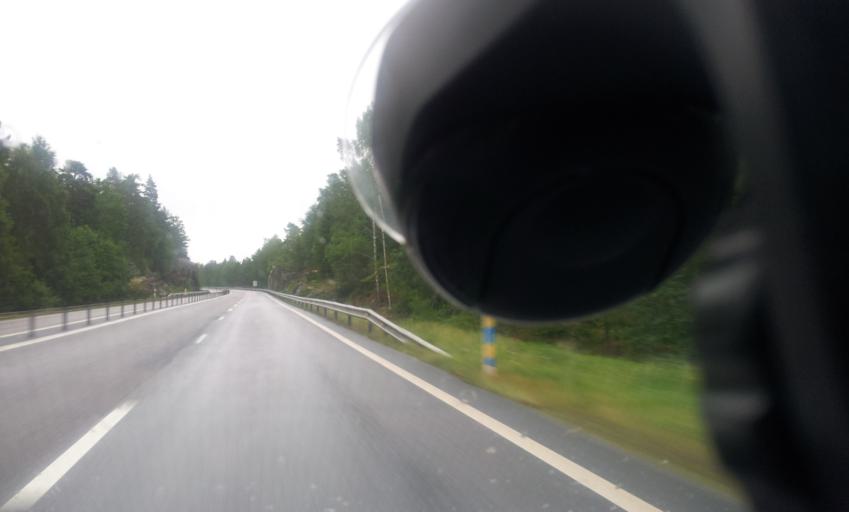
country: SE
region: OEstergoetland
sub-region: Valdemarsviks Kommun
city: Valdemarsvik
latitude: 58.0954
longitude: 16.5291
